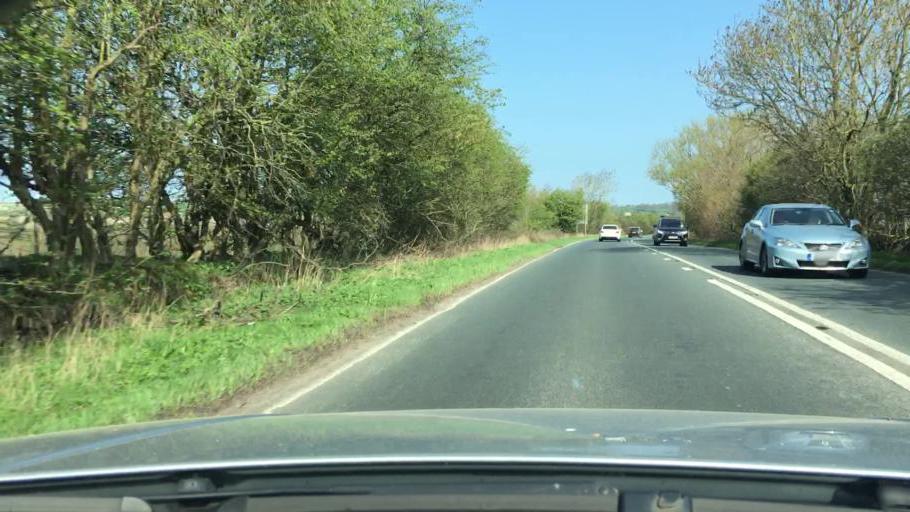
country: GB
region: England
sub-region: North Yorkshire
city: Pannal
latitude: 53.9406
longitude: -1.5371
